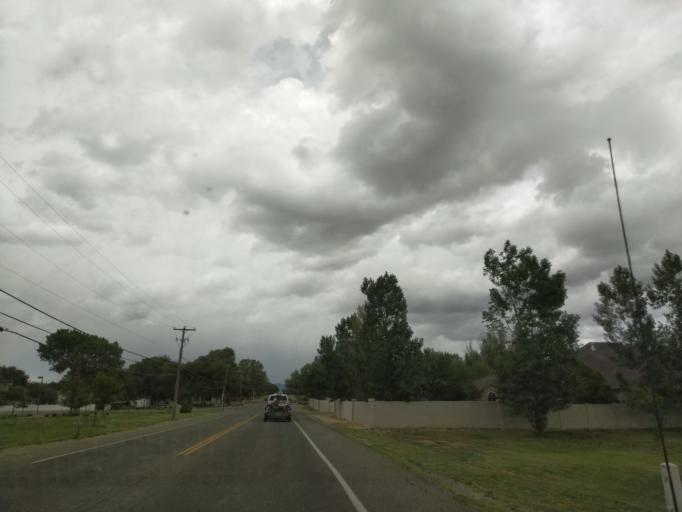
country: US
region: Colorado
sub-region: Mesa County
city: Grand Junction
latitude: 39.0970
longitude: -108.5616
